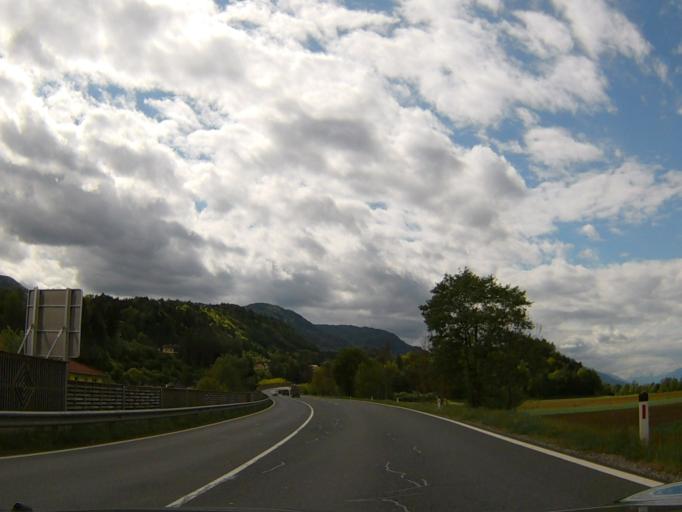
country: AT
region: Carinthia
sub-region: Politischer Bezirk Villach Land
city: Fresach
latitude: 46.6593
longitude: 13.7563
